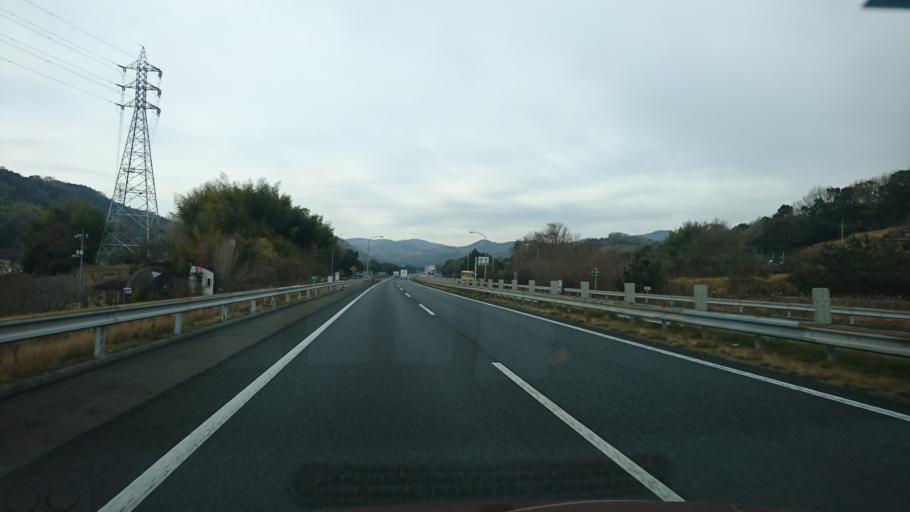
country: JP
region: Okayama
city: Kamogatacho-kamogata
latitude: 34.5518
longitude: 133.5908
